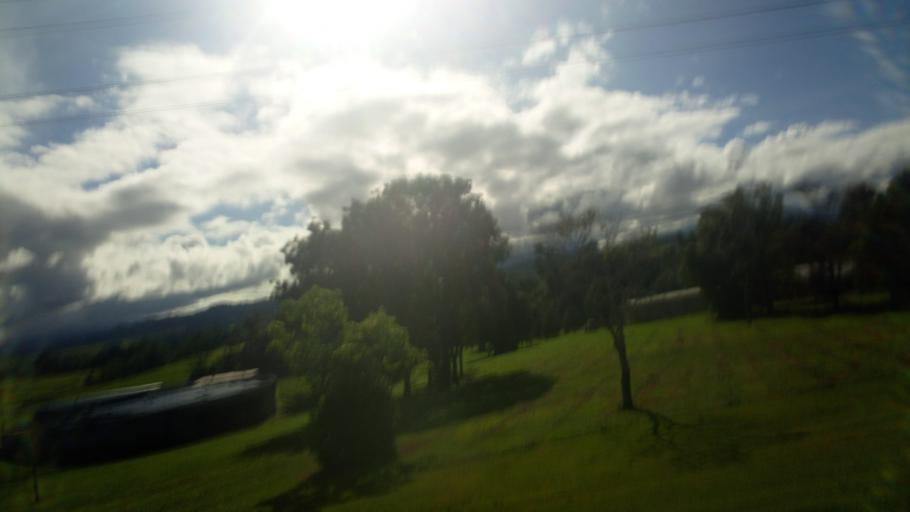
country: AU
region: Queensland
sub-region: Cassowary Coast
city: Innisfail
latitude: -17.5306
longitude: 145.9790
